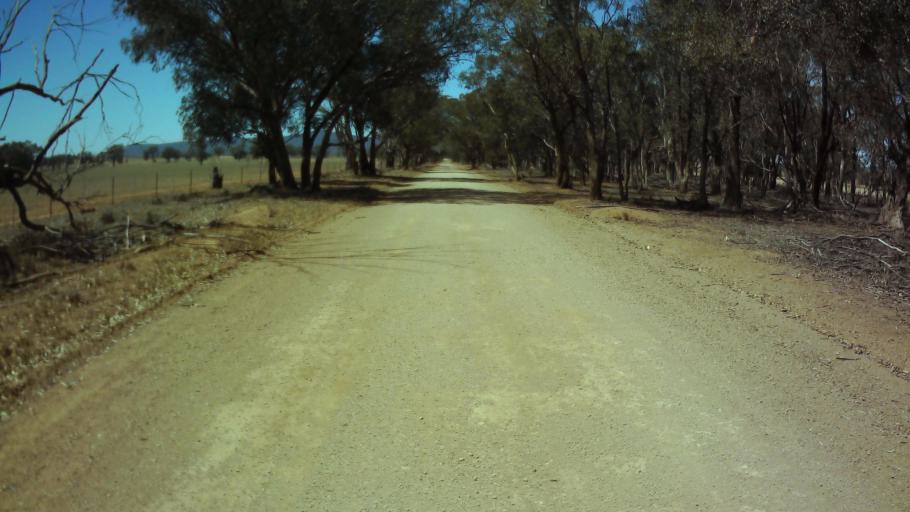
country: AU
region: New South Wales
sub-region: Weddin
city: Grenfell
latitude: -33.8964
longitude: 148.0845
